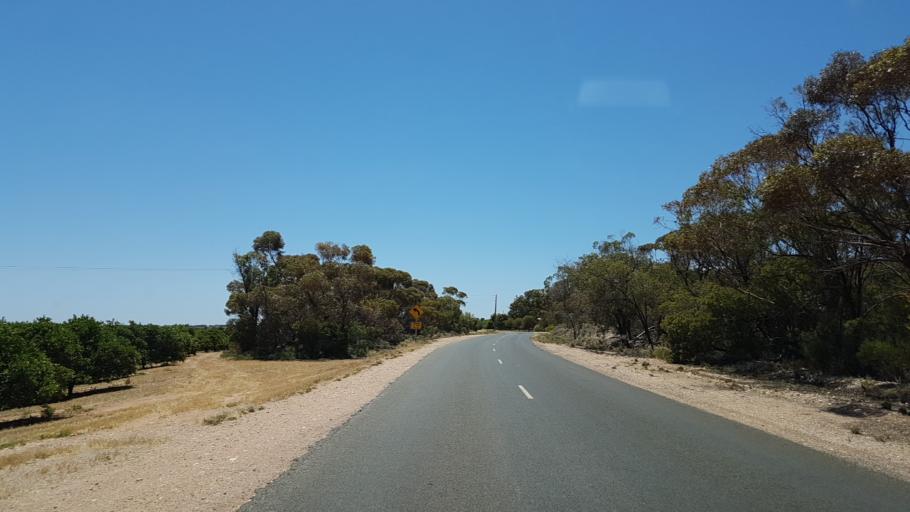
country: AU
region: South Australia
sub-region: Loxton Waikerie
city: Waikerie
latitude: -34.1793
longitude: 140.0254
